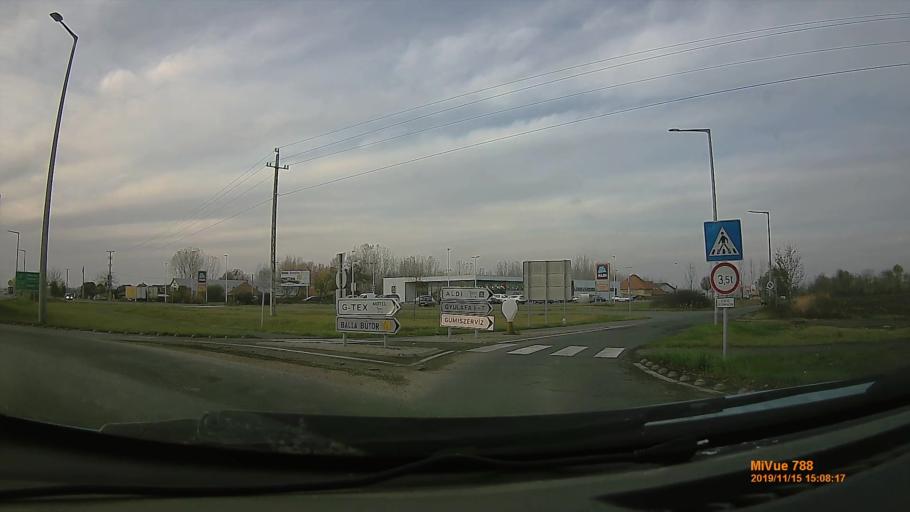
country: HU
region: Bekes
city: Gyula
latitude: 46.6532
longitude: 21.2380
